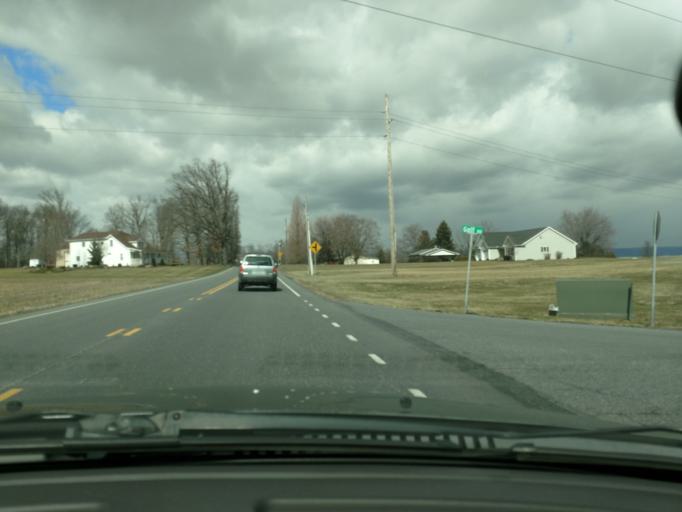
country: US
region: Pennsylvania
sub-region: Lebanon County
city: Myerstown
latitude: 40.4075
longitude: -76.3032
